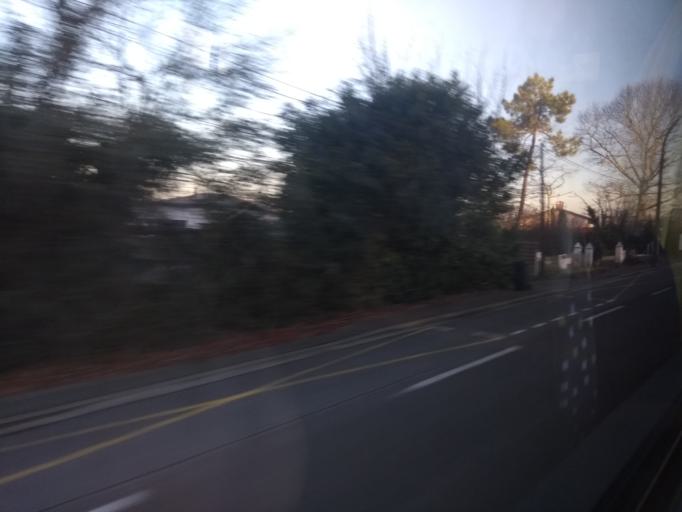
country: FR
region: Aquitaine
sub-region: Departement de la Gironde
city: Canejan
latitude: 44.7558
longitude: -0.6273
